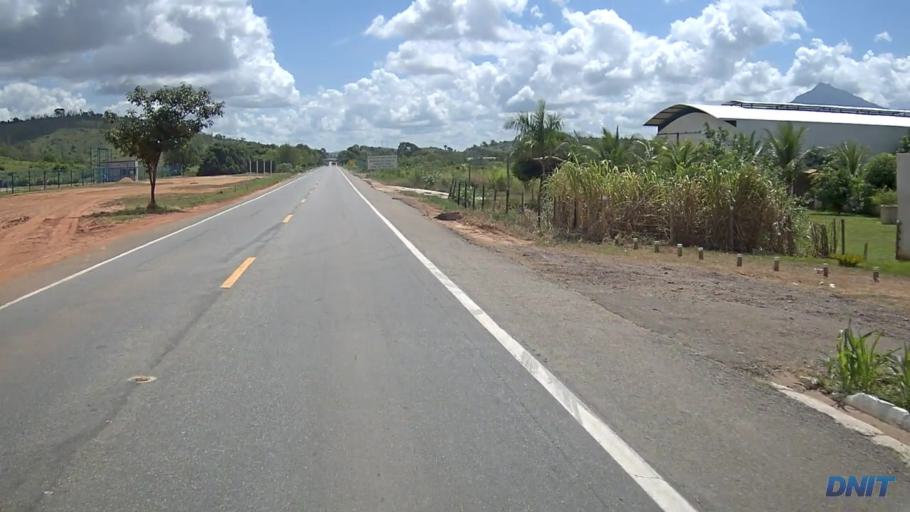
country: BR
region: Minas Gerais
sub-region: Governador Valadares
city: Governador Valadares
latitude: -18.9214
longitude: -42.0162
